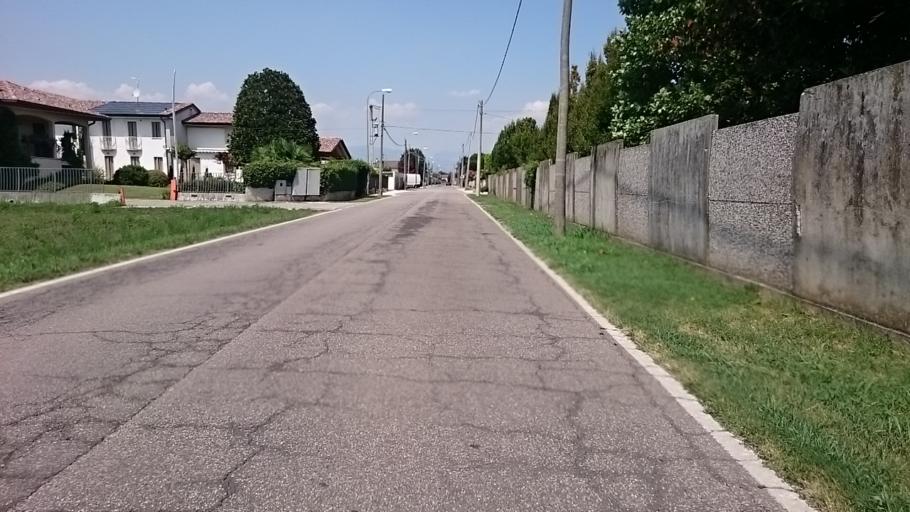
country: IT
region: Veneto
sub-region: Provincia di Padova
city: Fontaniva
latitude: 45.6570
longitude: 11.7577
